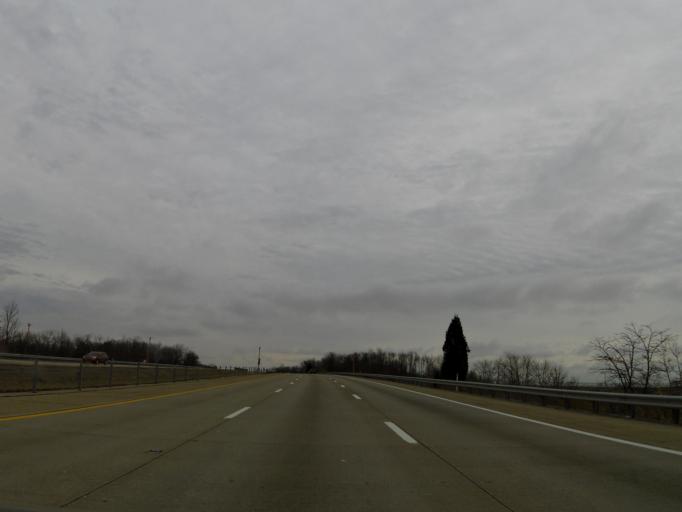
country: US
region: Kentucky
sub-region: Boone County
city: Hebron
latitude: 39.0764
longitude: -84.6856
